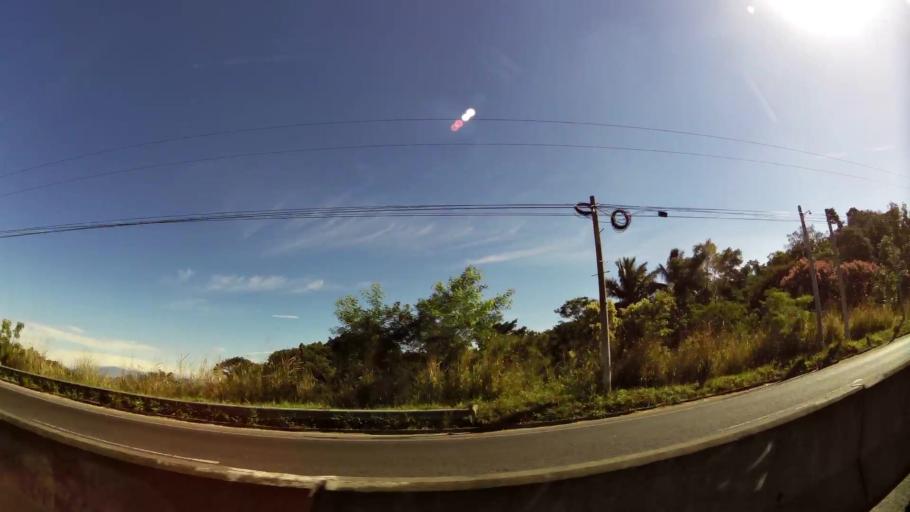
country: SV
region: Santa Ana
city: Coatepeque
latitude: 13.9338
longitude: -89.5238
